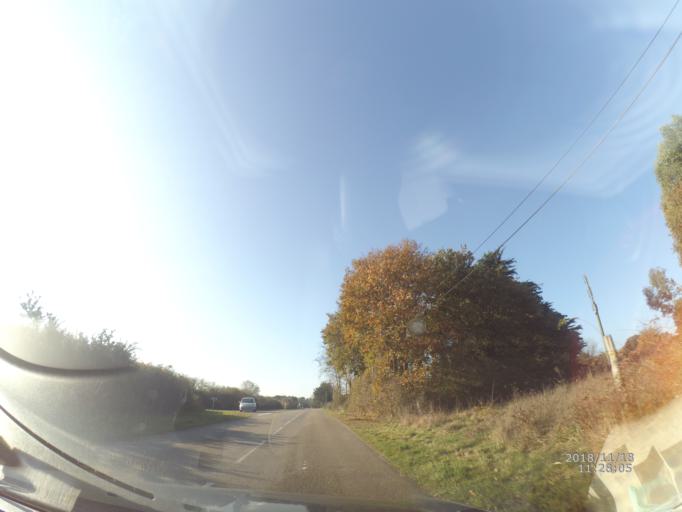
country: FR
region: Pays de la Loire
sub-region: Departement de la Loire-Atlantique
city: Saint-Michel-Chef-Chef
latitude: 47.2162
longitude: -2.1475
